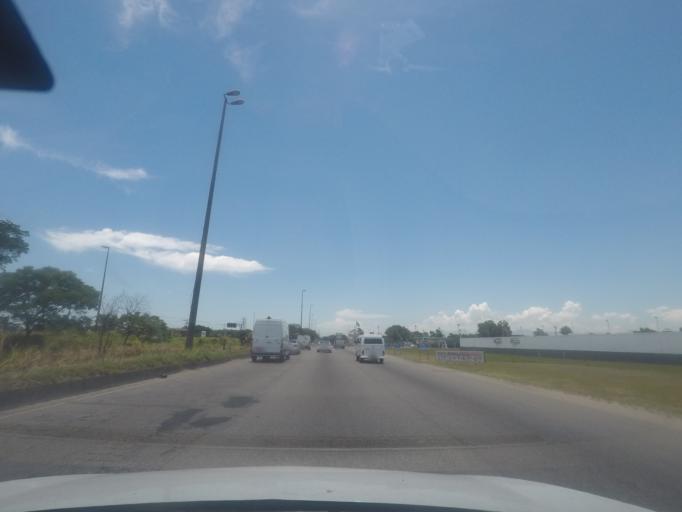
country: BR
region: Rio de Janeiro
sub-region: Itaguai
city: Itaguai
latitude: -22.8919
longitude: -43.6703
